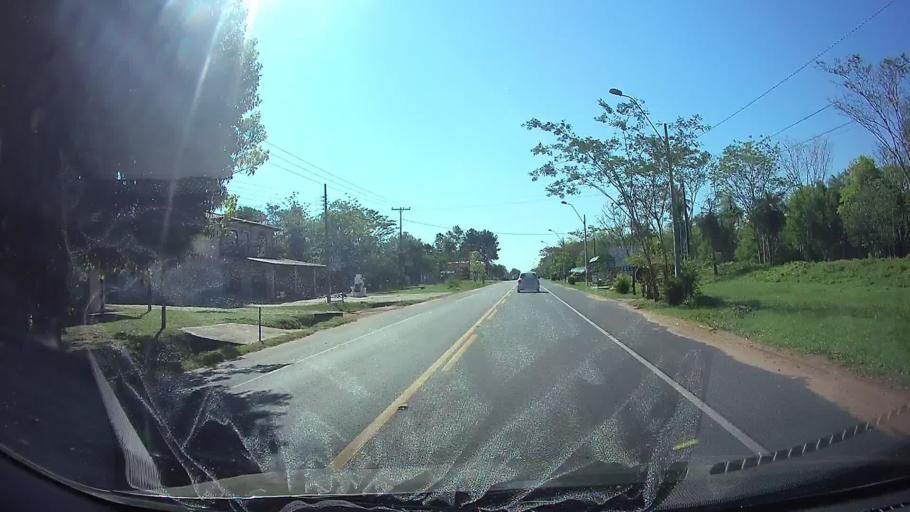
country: PY
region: Central
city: Aregua
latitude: -25.3215
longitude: -57.3689
